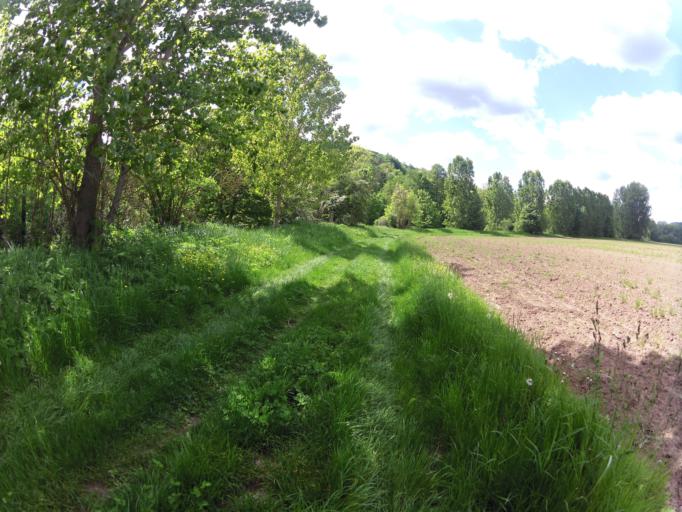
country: DE
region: Thuringia
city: Treffurt
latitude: 51.1119
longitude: 10.2529
